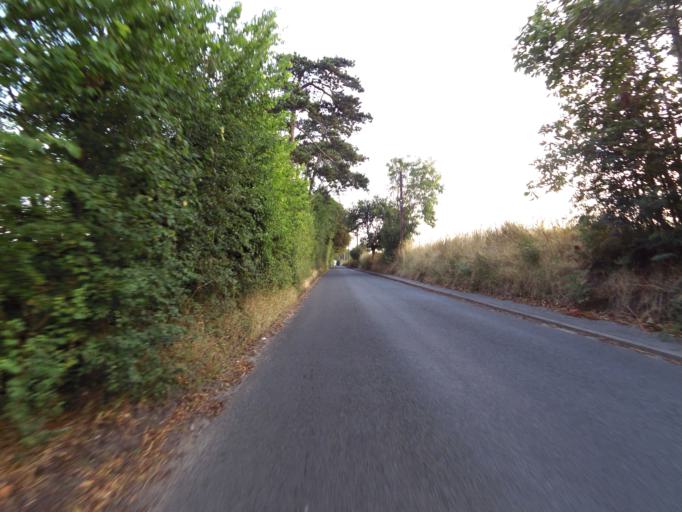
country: GB
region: England
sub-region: Suffolk
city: Bramford
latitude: 52.0796
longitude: 1.1057
